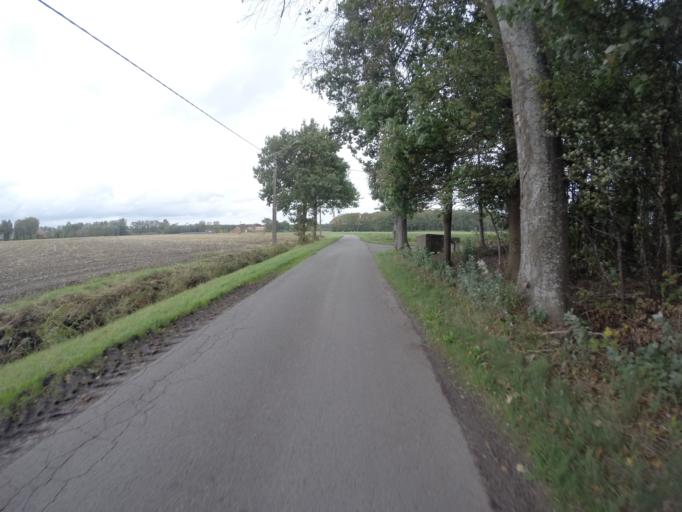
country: BE
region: Flanders
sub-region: Provincie Oost-Vlaanderen
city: Aalter
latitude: 51.0910
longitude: 3.4151
